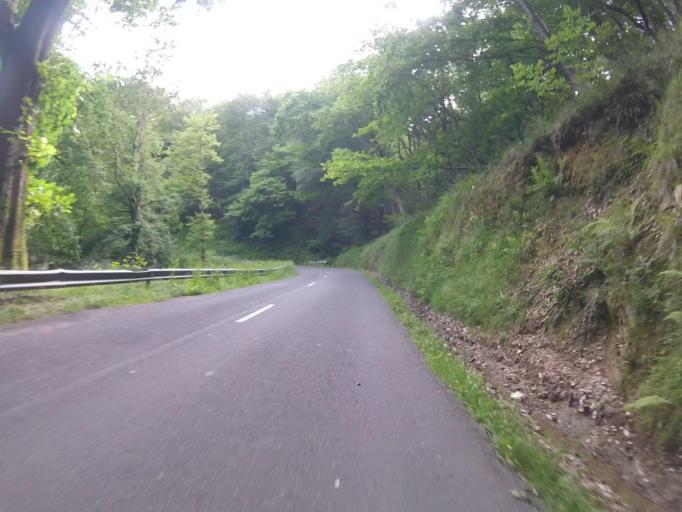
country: ES
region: Basque Country
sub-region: Provincia de Guipuzcoa
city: Errenteria
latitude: 43.2712
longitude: -1.8461
